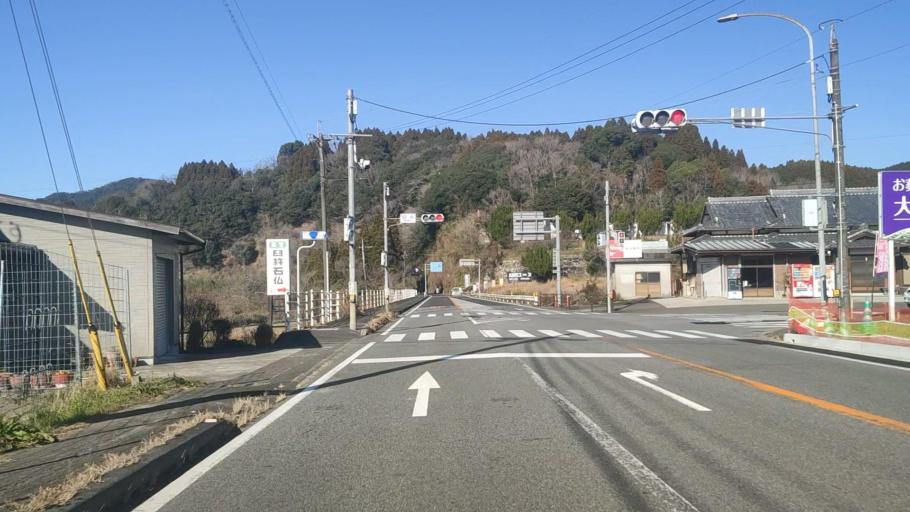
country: JP
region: Oita
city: Usuki
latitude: 33.0522
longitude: 131.6890
